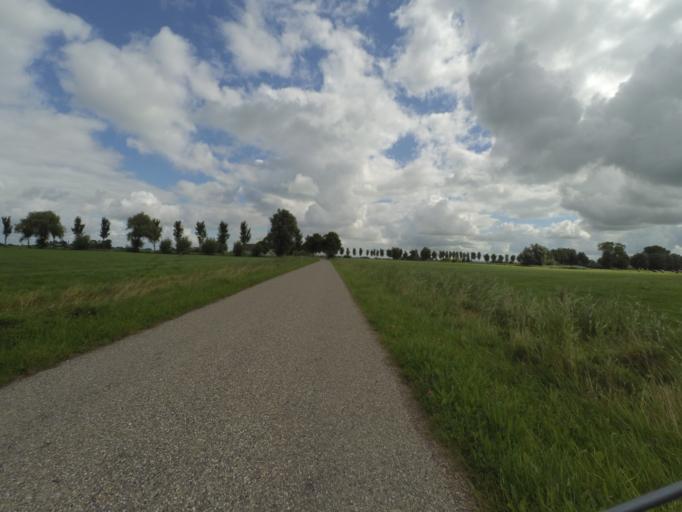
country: NL
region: Friesland
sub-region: Gemeente Kollumerland en Nieuwkruisland
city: Kollum
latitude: 53.2708
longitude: 6.1883
